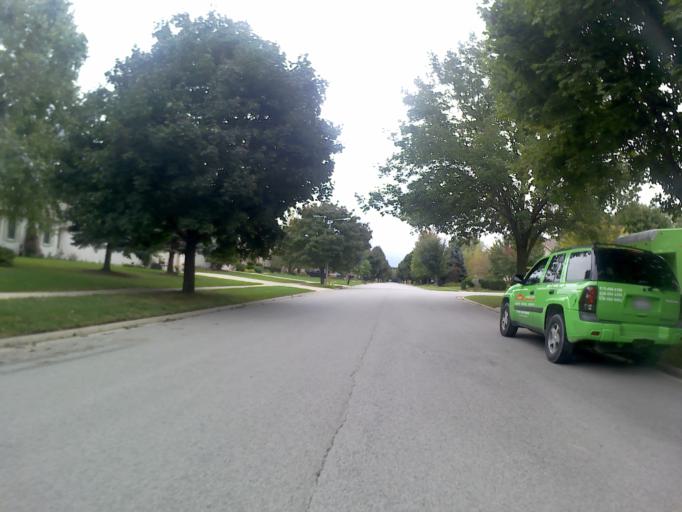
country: US
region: Illinois
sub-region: Kendall County
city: Lynwood
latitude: 41.6917
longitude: -88.3743
